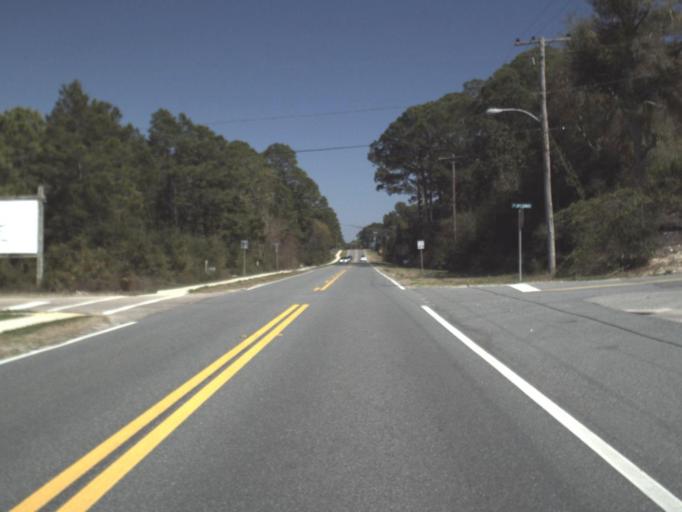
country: US
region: Florida
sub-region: Franklin County
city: Carrabelle
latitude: 29.8501
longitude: -84.6540
